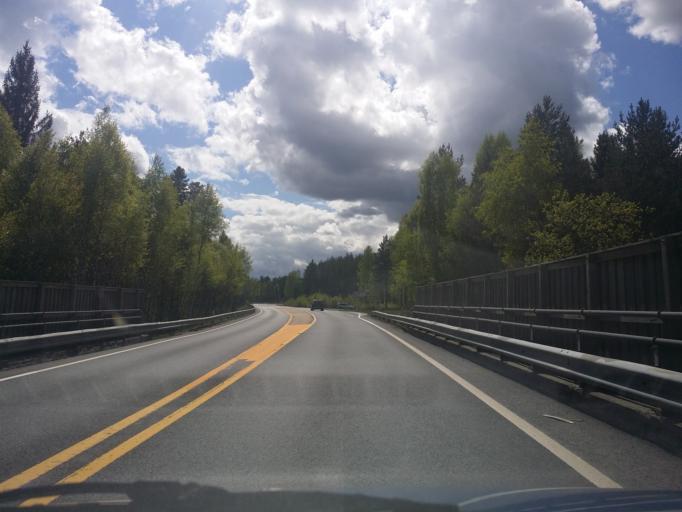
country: NO
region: Buskerud
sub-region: Modum
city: Vikersund
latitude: 59.9461
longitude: 9.9679
